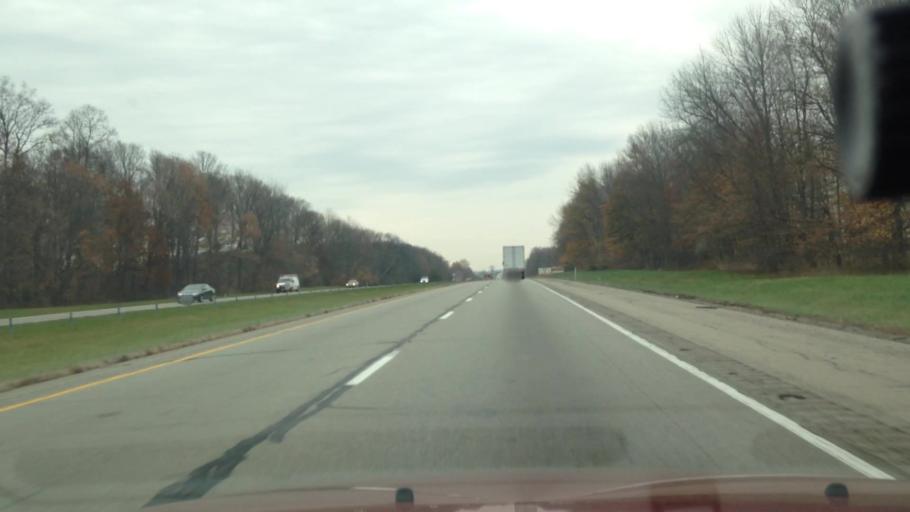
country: US
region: Indiana
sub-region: Wayne County
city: Cambridge City
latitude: 39.8534
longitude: -85.2172
